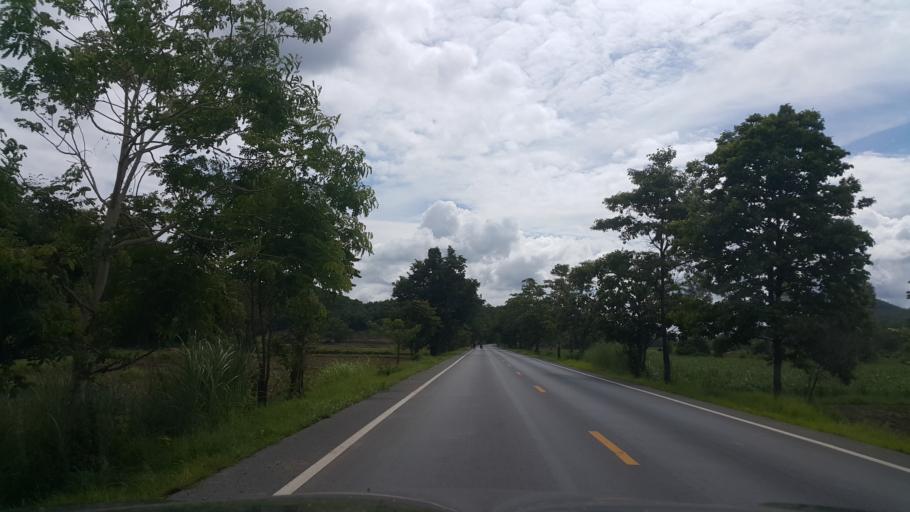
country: TH
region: Uttaradit
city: Thong Saen Khan
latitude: 17.3681
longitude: 100.2520
